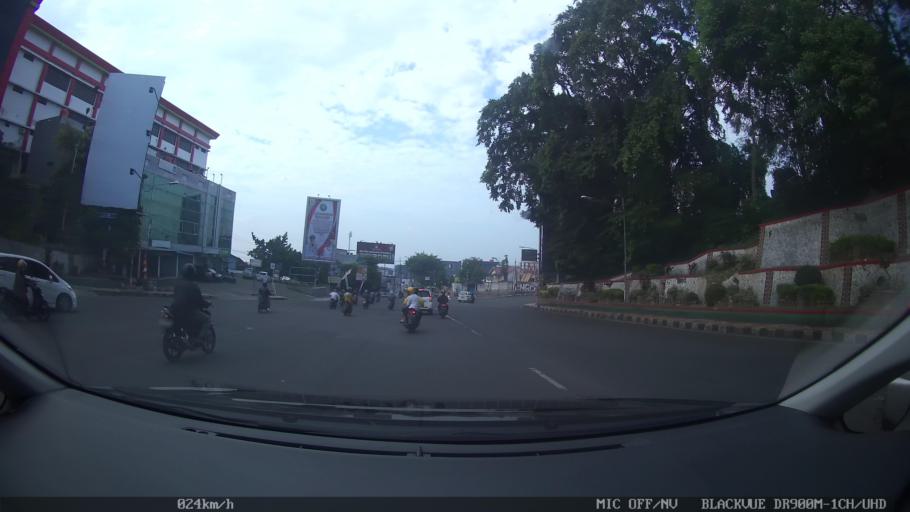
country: ID
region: Lampung
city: Bandarlampung
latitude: -5.4297
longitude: 105.2615
